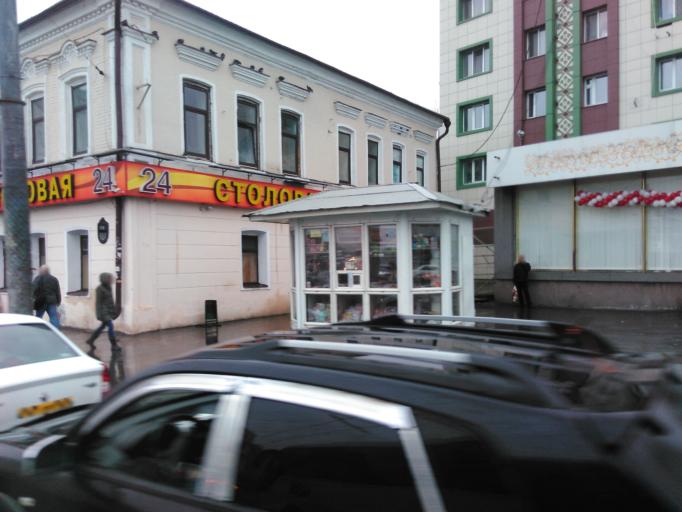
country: RU
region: Tatarstan
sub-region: Gorod Kazan'
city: Kazan
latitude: 55.7894
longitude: 49.1016
